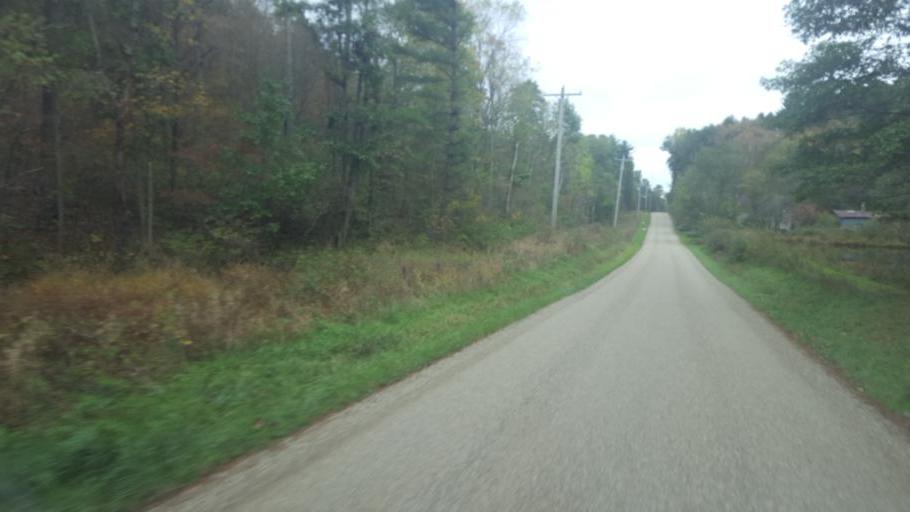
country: US
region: Ohio
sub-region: Ashland County
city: Loudonville
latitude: 40.5768
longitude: -82.2444
